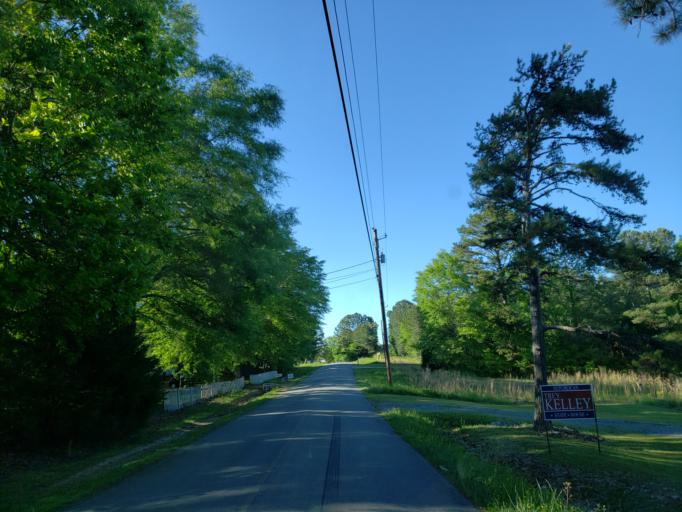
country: US
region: Georgia
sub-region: Polk County
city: Aragon
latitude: 34.0140
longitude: -85.1453
